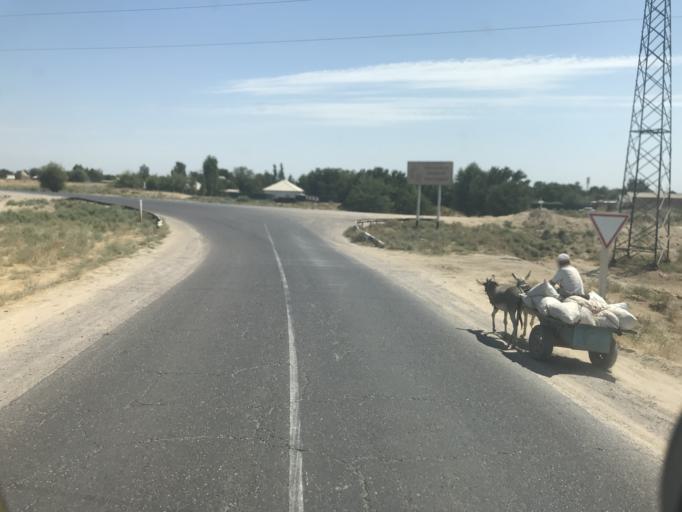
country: UZ
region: Toshkent
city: Yangiyul
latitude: 41.3282
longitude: 68.8928
